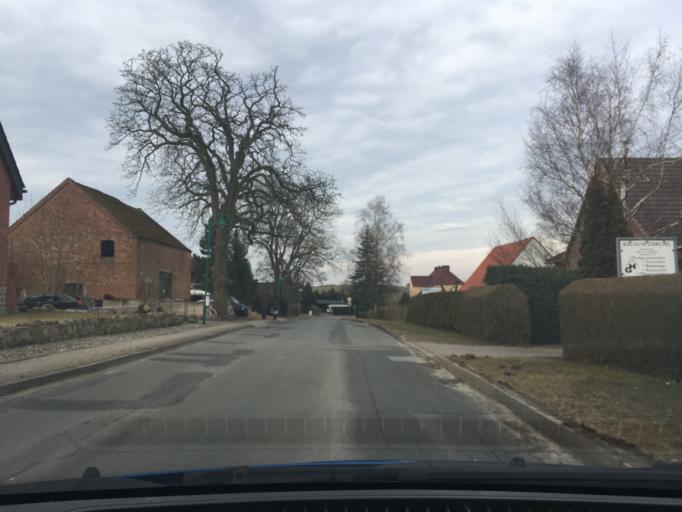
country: DE
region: Mecklenburg-Vorpommern
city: Klein Rogahn
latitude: 53.5983
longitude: 11.3297
